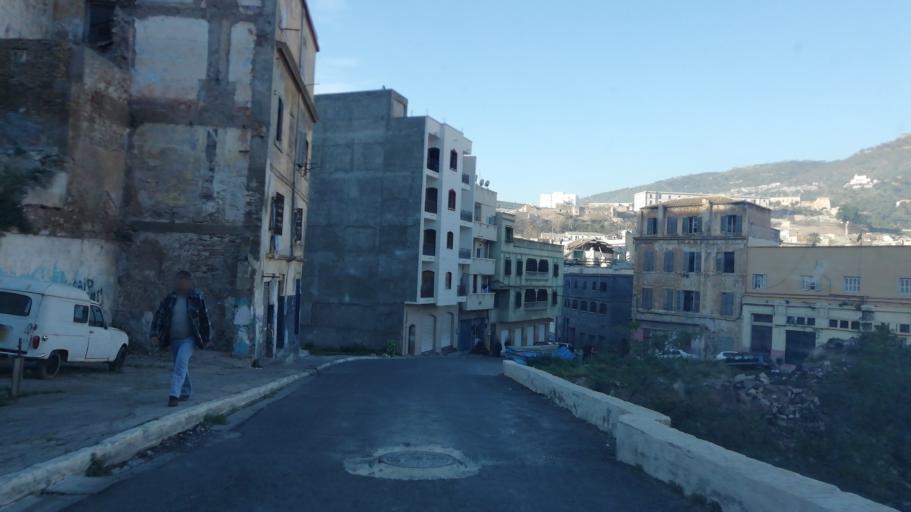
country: DZ
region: Oran
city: Oran
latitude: 35.7046
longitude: -0.6509
